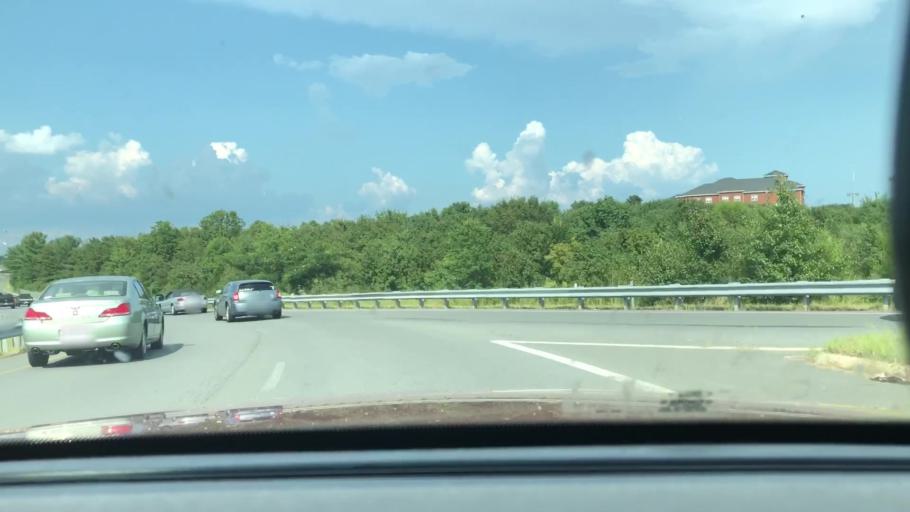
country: US
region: Virginia
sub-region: Fairfax County
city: Chantilly
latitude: 38.8861
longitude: -77.4464
